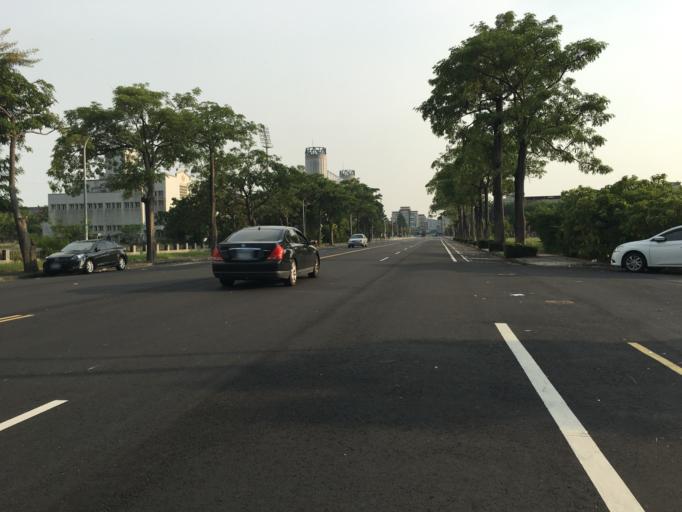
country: TW
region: Taiwan
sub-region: Chiayi
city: Taibao
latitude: 23.4597
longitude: 120.2887
